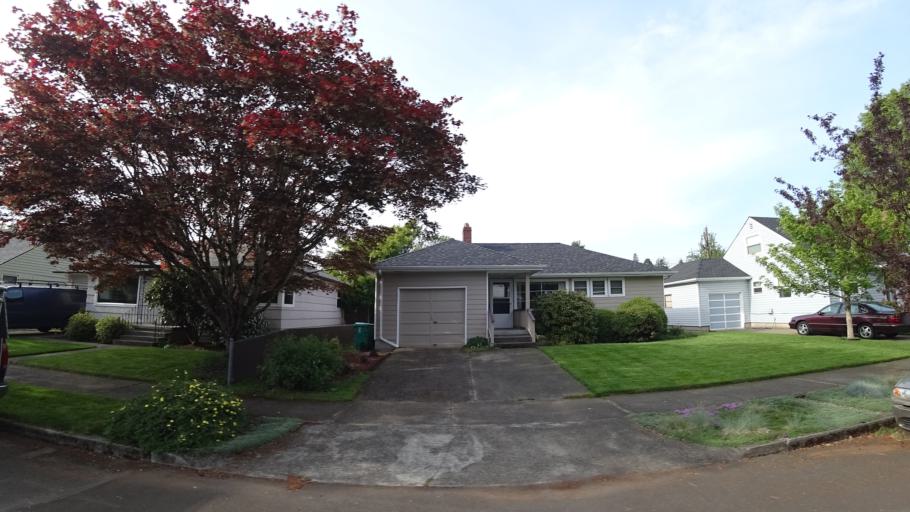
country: US
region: Oregon
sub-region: Clackamas County
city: Milwaukie
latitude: 45.4677
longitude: -122.6209
